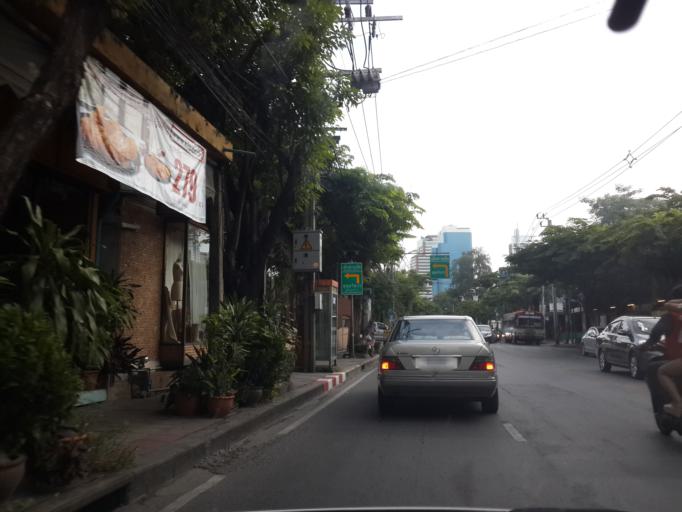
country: TH
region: Bangkok
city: Watthana
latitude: 13.7297
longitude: 100.5861
